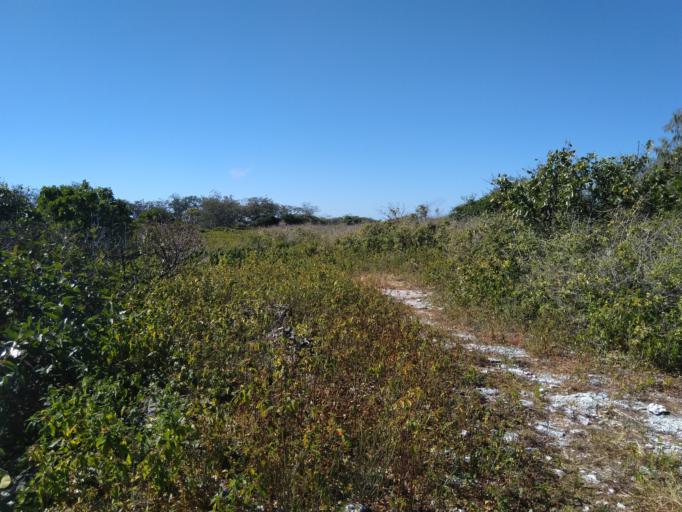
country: AU
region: Queensland
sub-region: Bundaberg
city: Bundaberg
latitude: -24.1111
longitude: 152.7146
